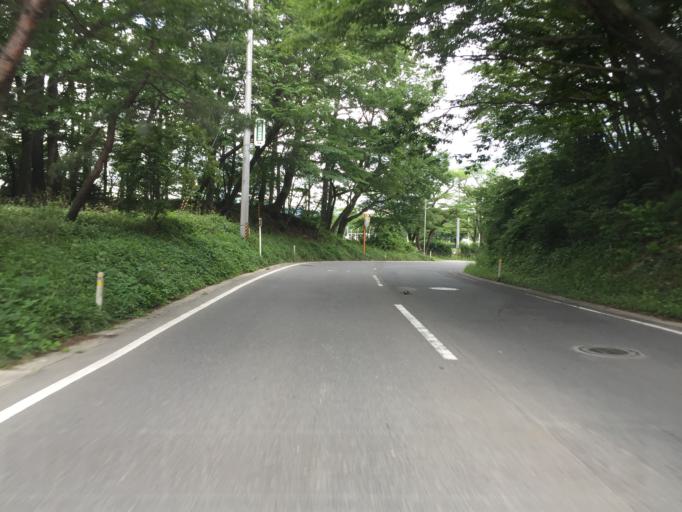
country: JP
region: Fukushima
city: Namie
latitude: 37.6214
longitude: 140.9598
